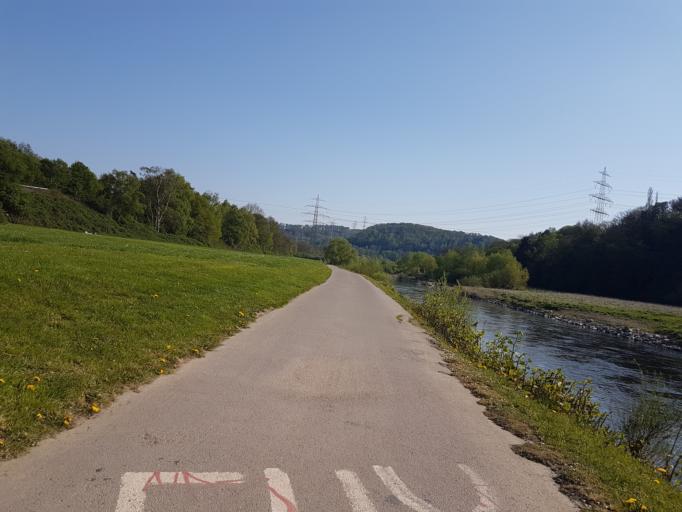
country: DE
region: North Rhine-Westphalia
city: Hattingen
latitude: 51.4000
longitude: 7.1620
